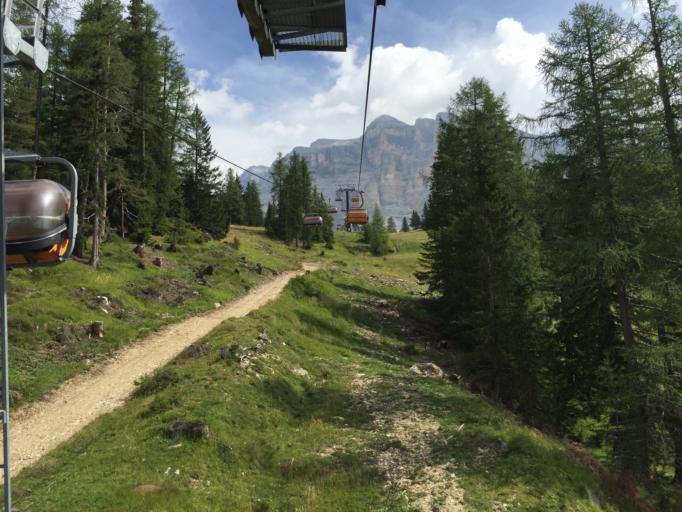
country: IT
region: Trentino-Alto Adige
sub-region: Bolzano
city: Badia
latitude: 46.6120
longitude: 11.9196
